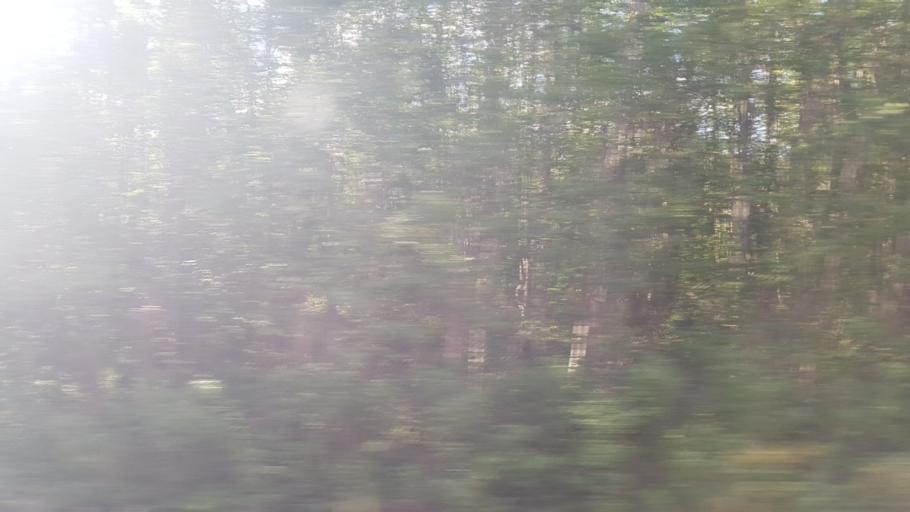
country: NO
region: Sor-Trondelag
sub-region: Midtre Gauldal
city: Storen
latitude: 63.0358
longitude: 10.2851
